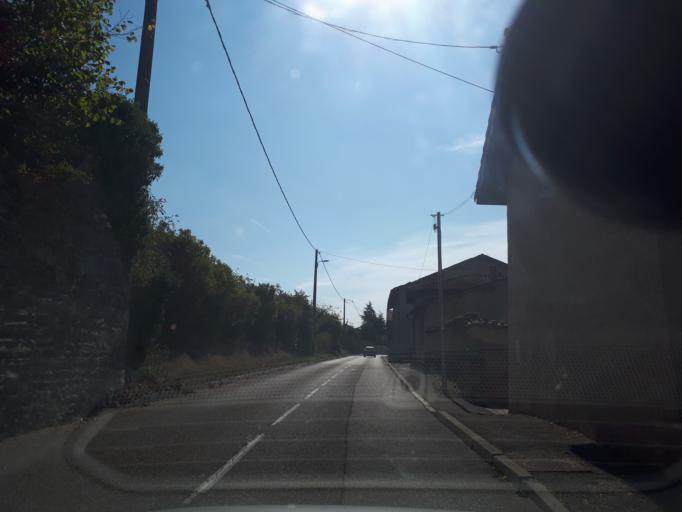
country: FR
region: Rhone-Alpes
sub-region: Departement de l'Isere
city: Chatonnay
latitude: 45.5125
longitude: 5.2024
